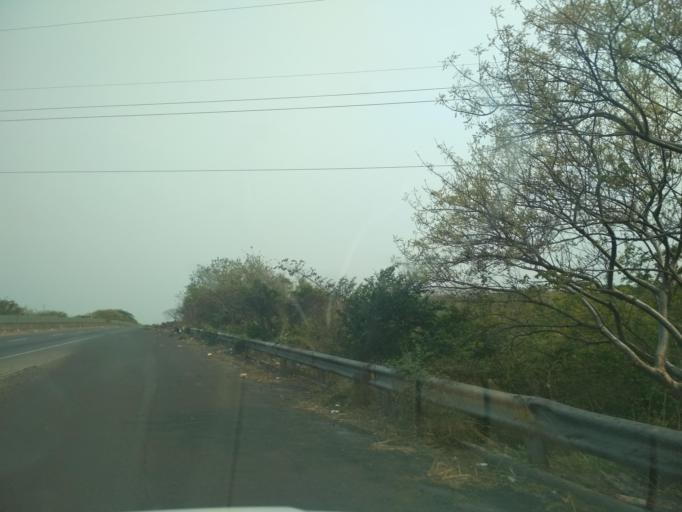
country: MX
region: Veracruz
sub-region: Veracruz
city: Las Amapolas
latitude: 19.1342
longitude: -96.2512
